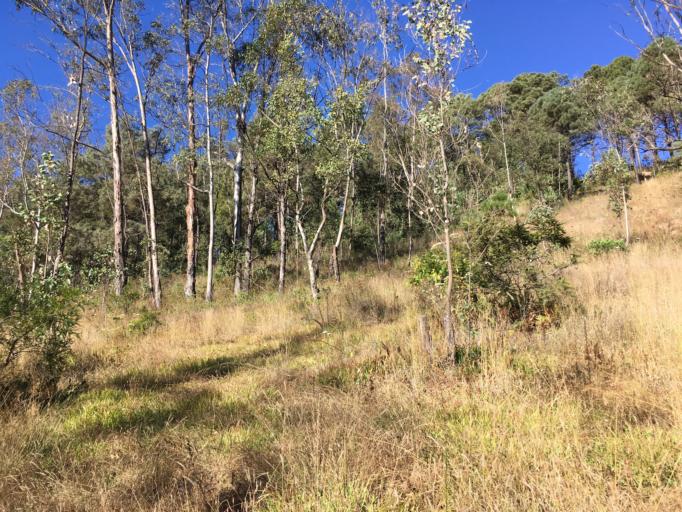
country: MX
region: Michoacan
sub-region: Morelia
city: Montana Monarca (Punta Altozano)
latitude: 19.6595
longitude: -101.1456
